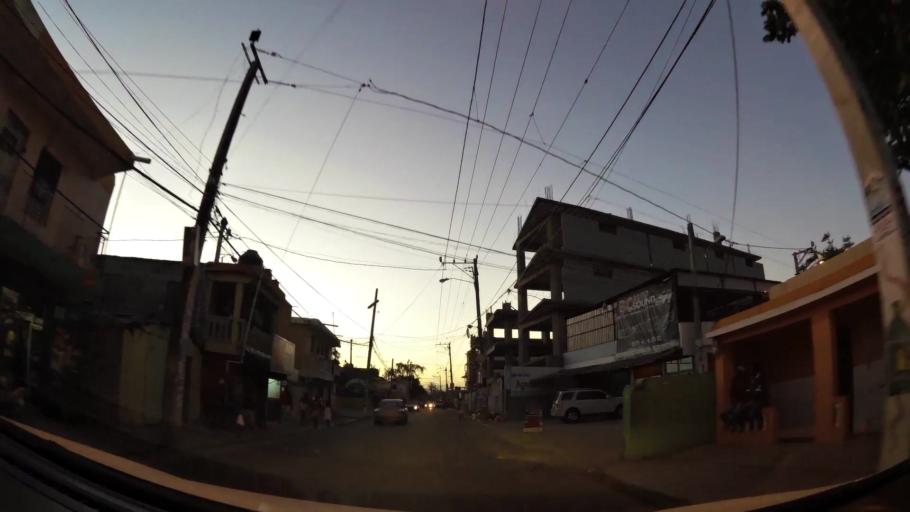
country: DO
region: Santo Domingo
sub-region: Santo Domingo
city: Santo Domingo Este
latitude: 18.4999
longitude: -69.8373
